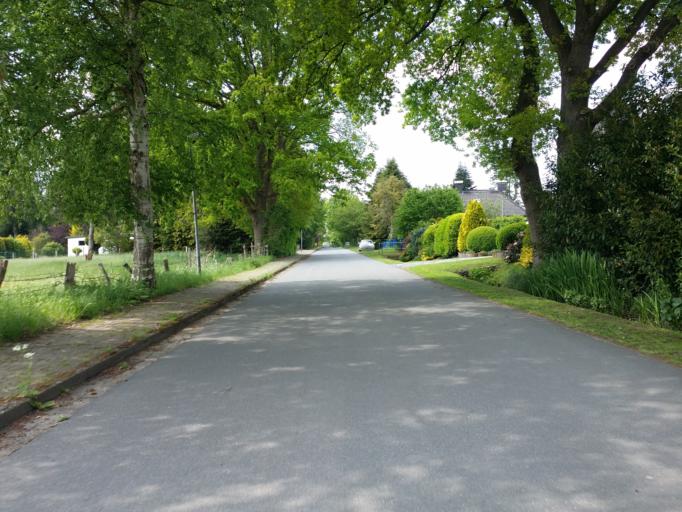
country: DE
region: Lower Saxony
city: Hambergen
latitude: 53.2912
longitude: 8.8232
